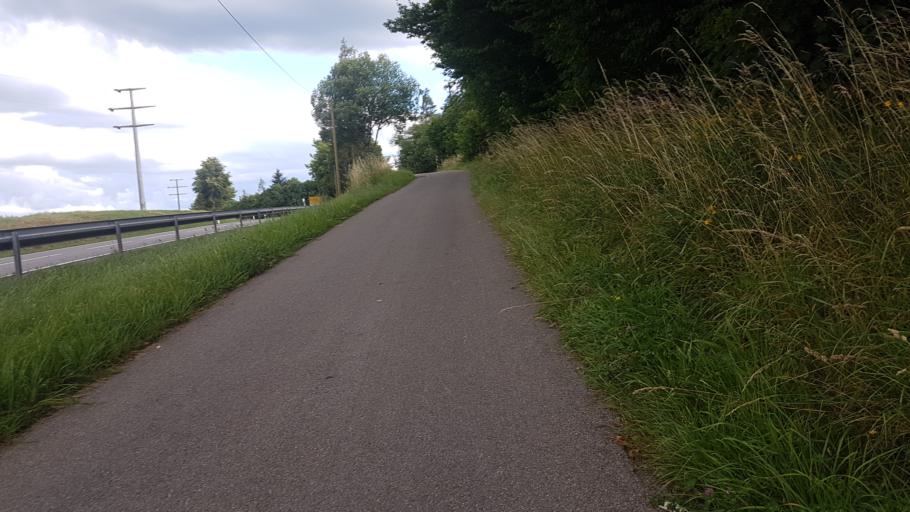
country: DE
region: Baden-Wuerttemberg
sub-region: Freiburg Region
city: Unterkirnach
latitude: 48.0079
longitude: 8.4092
